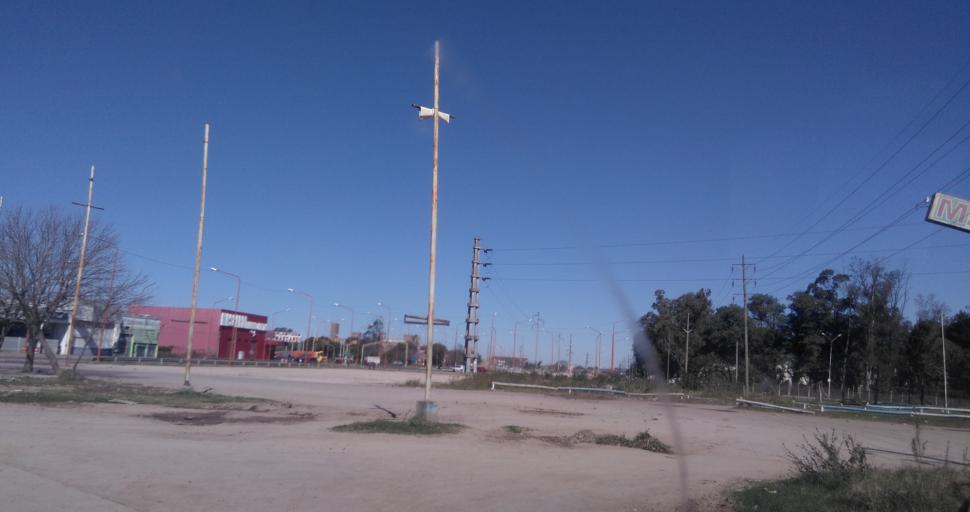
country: AR
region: Chaco
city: Fontana
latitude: -27.4283
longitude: -59.0104
